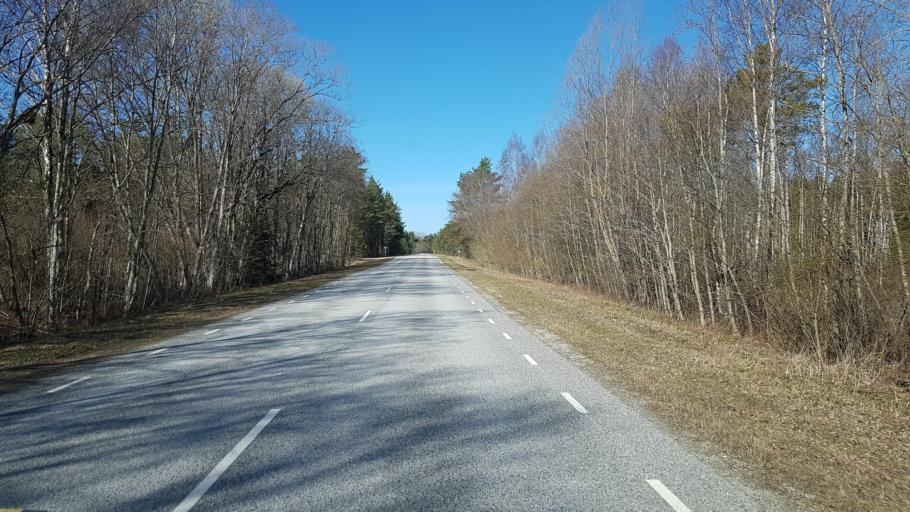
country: EE
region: Laeaene
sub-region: Lihula vald
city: Lihula
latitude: 58.5693
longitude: 23.7613
